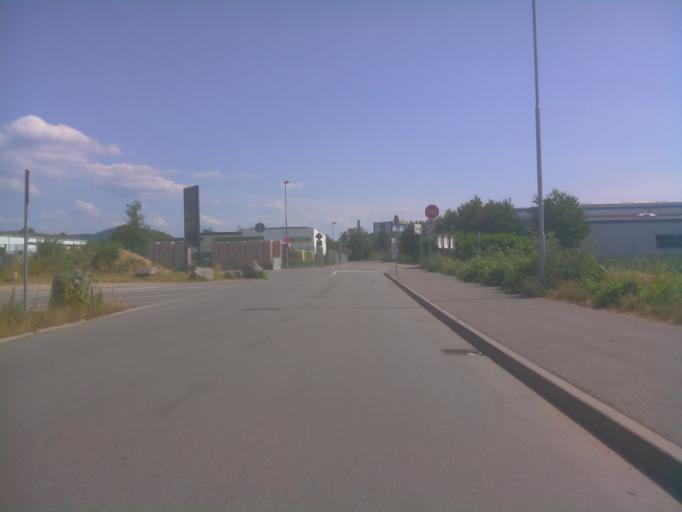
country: DE
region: Baden-Wuerttemberg
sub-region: Karlsruhe Region
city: Heddesheim
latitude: 49.5112
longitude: 8.6288
